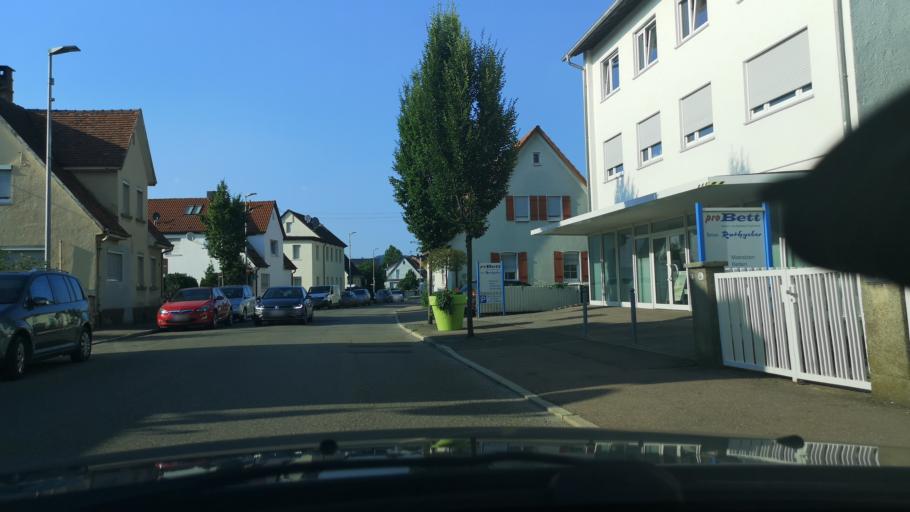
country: DE
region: Baden-Wuerttemberg
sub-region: Regierungsbezirk Stuttgart
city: Salach
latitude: 48.6870
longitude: 9.7347
